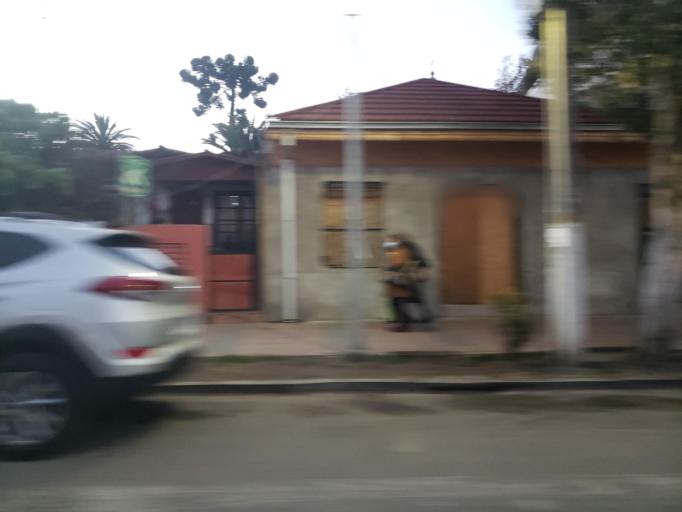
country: CL
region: Santiago Metropolitan
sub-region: Provincia de Talagante
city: El Monte
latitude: -33.6789
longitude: -70.9785
